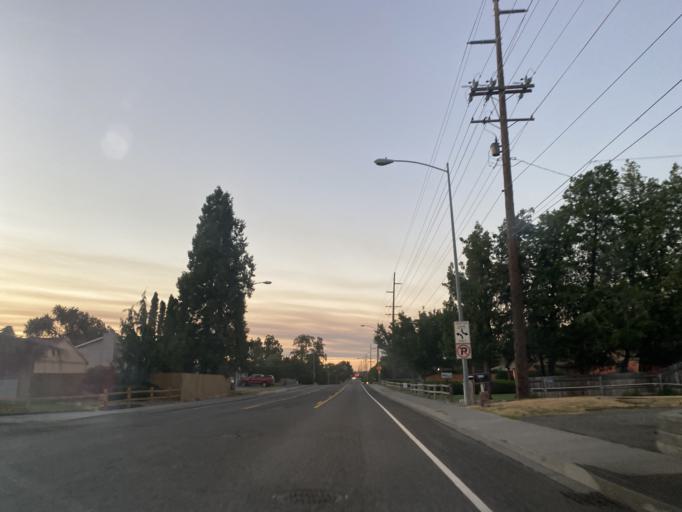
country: US
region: Washington
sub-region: Benton County
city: Kennewick
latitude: 46.2006
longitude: -119.1695
